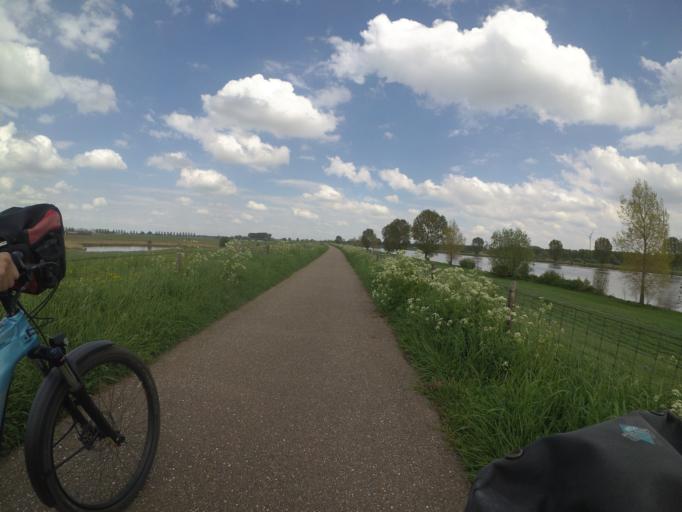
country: NL
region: North Brabant
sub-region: Gemeente Waalwijk
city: Waalwijk
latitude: 51.7146
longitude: 5.0597
